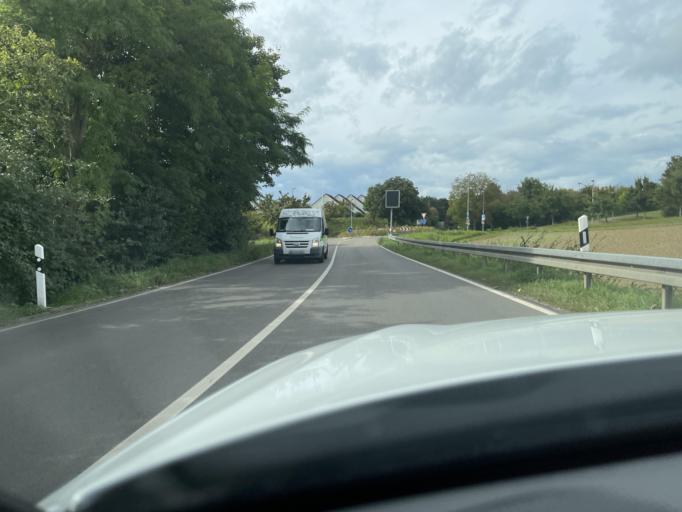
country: DE
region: Baden-Wuerttemberg
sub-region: Regierungsbezirk Stuttgart
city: Marbach am Neckar
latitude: 48.9316
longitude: 9.2658
